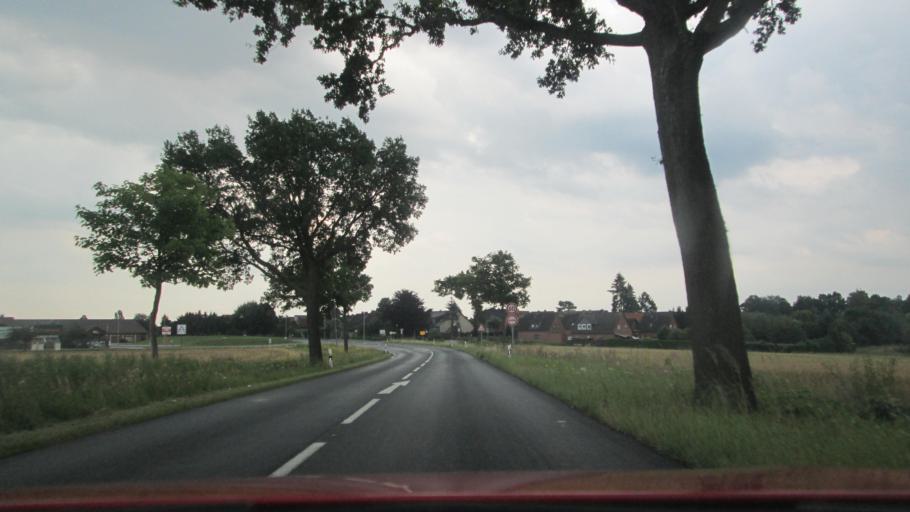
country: DE
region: Lower Saxony
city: Wolfsburg
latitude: 52.3648
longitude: 10.7476
